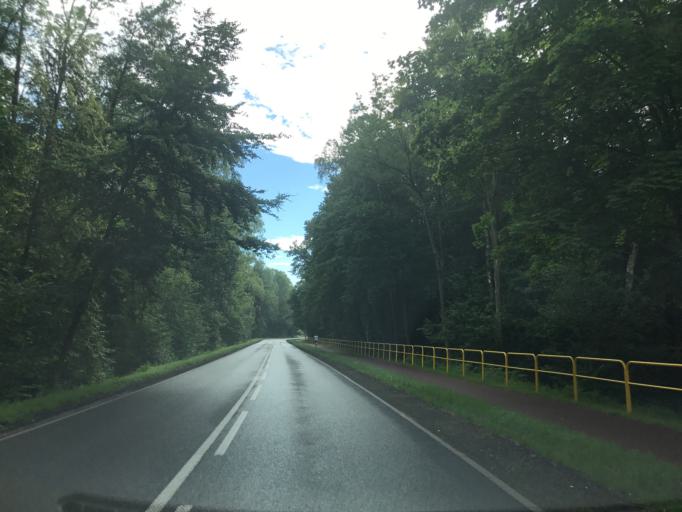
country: PL
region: West Pomeranian Voivodeship
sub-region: Powiat koszalinski
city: Sianow
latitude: 54.2099
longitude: 16.2596
